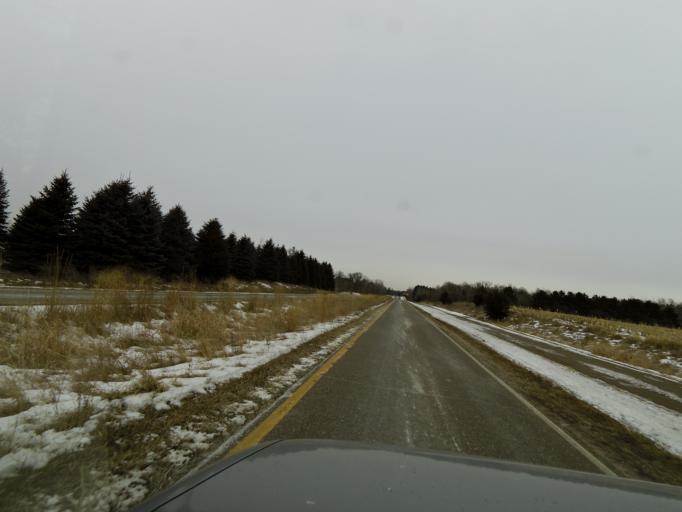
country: US
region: Minnesota
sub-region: Washington County
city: Lake Elmo
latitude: 44.9660
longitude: -92.9034
